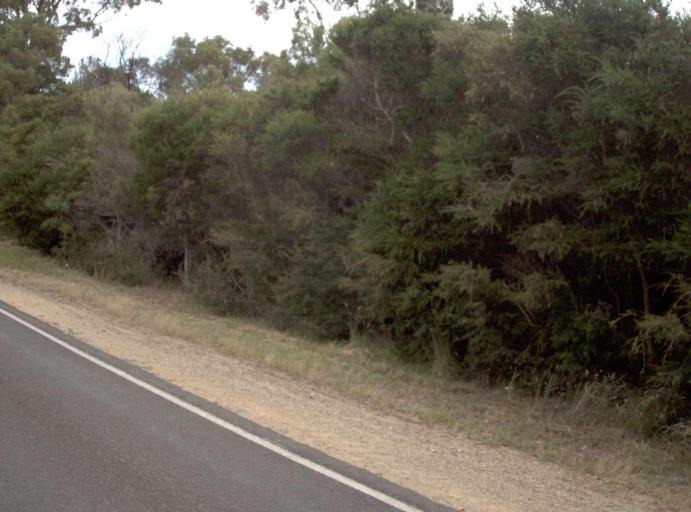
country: AU
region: Victoria
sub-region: Wellington
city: Sale
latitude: -38.1861
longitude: 147.0919
